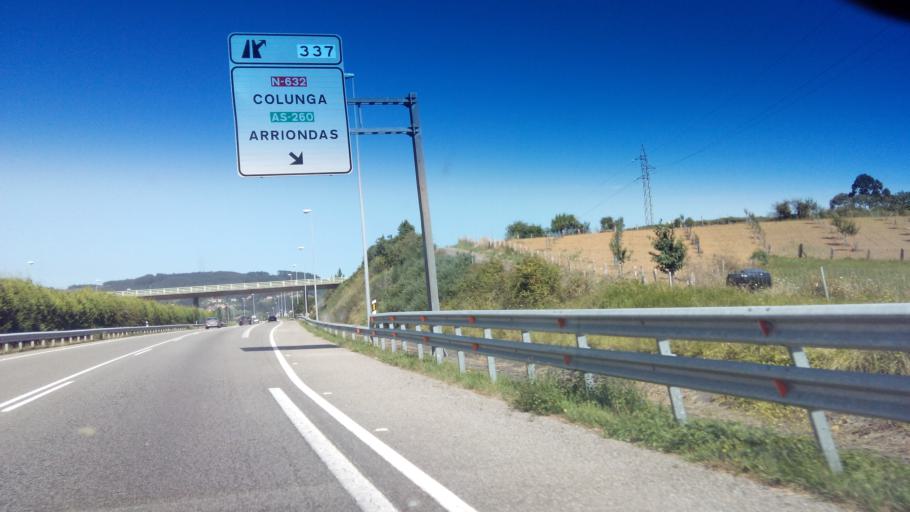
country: ES
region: Asturias
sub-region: Province of Asturias
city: Colunga
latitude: 43.4762
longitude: -5.2502
